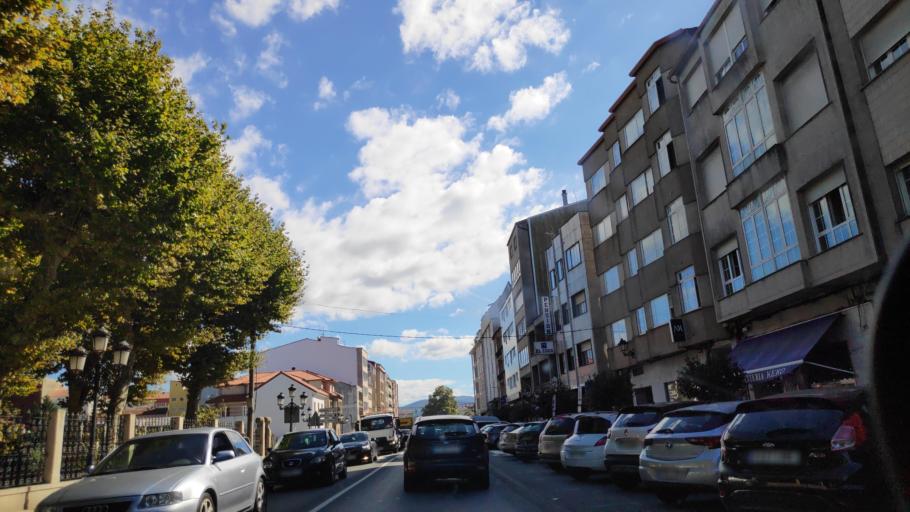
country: ES
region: Galicia
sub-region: Provincia da Coruna
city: Padron
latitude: 42.7387
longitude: -8.6592
